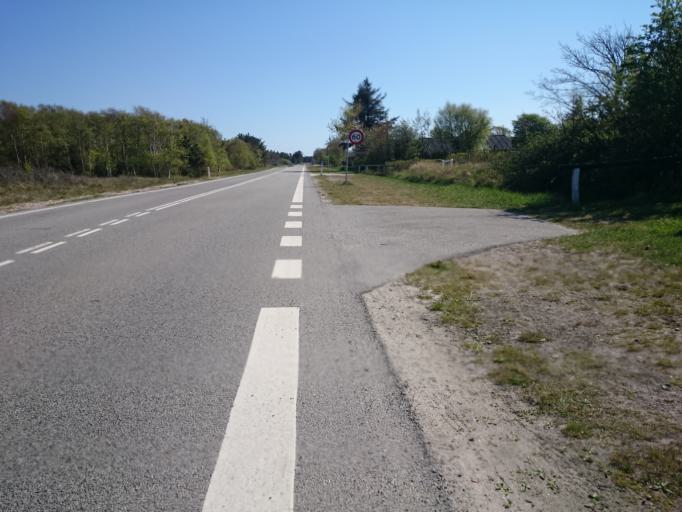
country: DK
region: North Denmark
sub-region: Frederikshavn Kommune
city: Skagen
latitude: 57.7365
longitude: 10.6032
